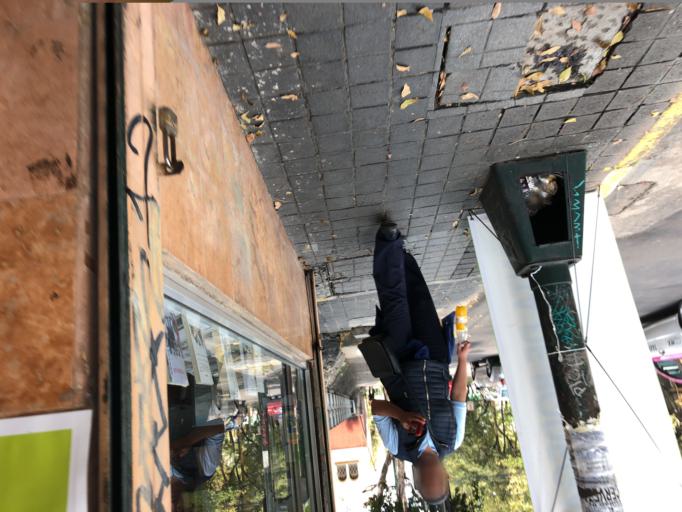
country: MX
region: Mexico City
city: Coyoacan
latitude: 19.3345
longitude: -99.1766
